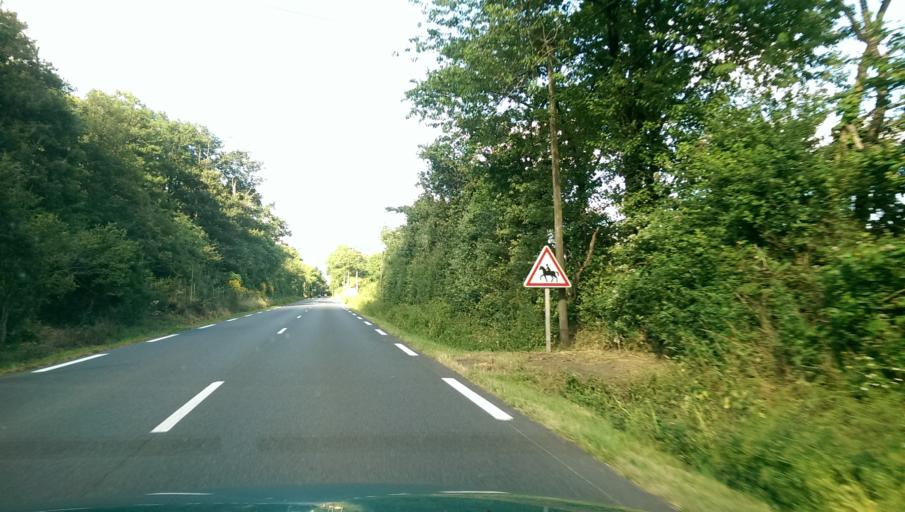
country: FR
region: Pays de la Loire
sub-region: Departement de la Vendee
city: Rocheserviere
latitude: 46.9283
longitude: -1.5238
